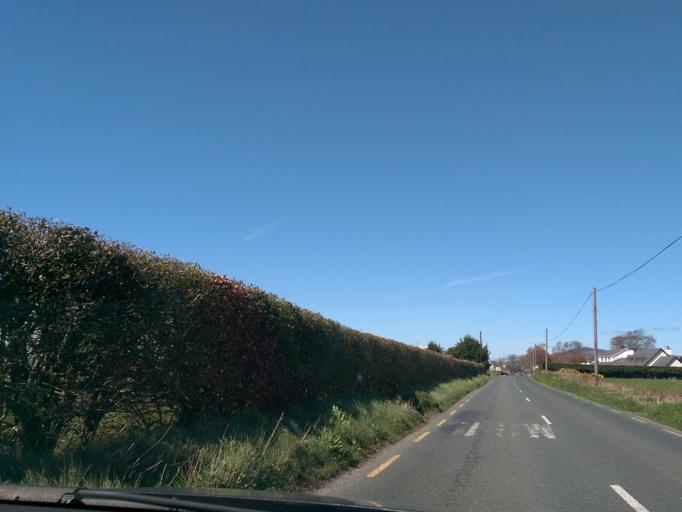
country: IE
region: Leinster
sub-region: Wicklow
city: Carnew
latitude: 52.8583
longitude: -6.5514
